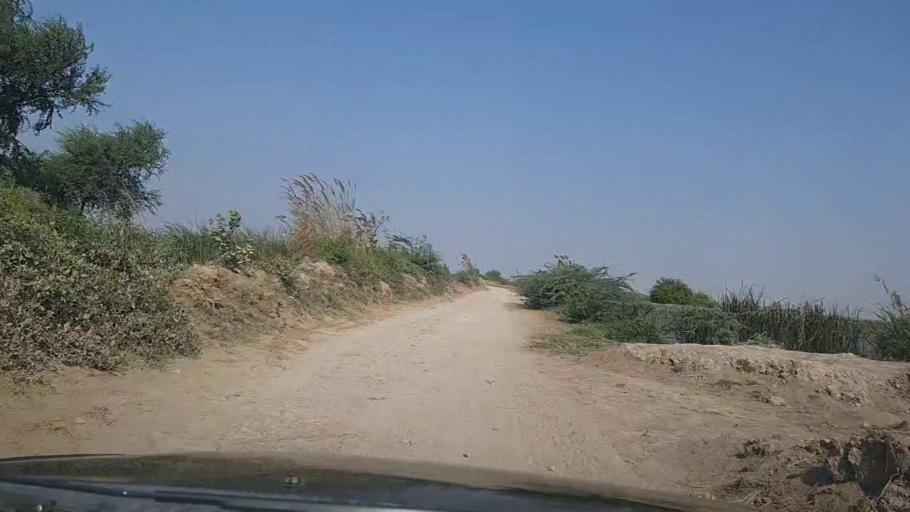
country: PK
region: Sindh
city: Thatta
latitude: 24.6358
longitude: 67.8136
